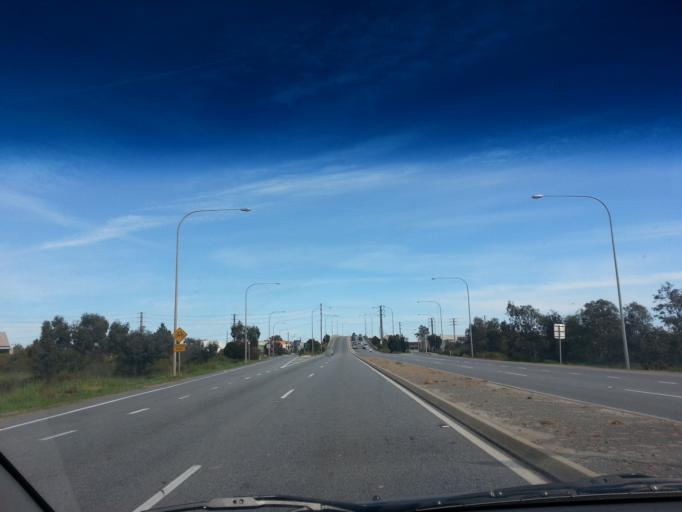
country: AU
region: South Australia
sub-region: Port Adelaide Enfield
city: Alberton
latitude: -34.8370
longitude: 138.5255
